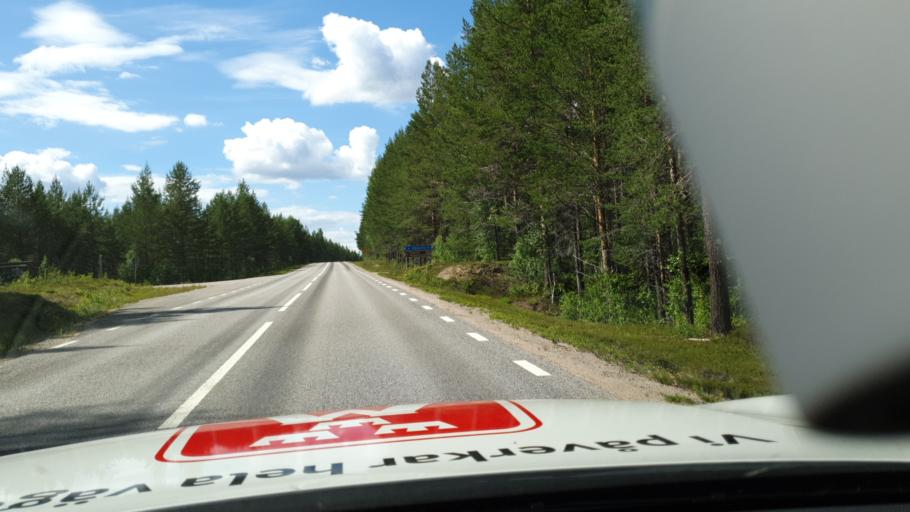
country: SE
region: Jaemtland
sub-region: Harjedalens Kommun
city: Sveg
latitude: 62.0136
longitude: 14.8770
